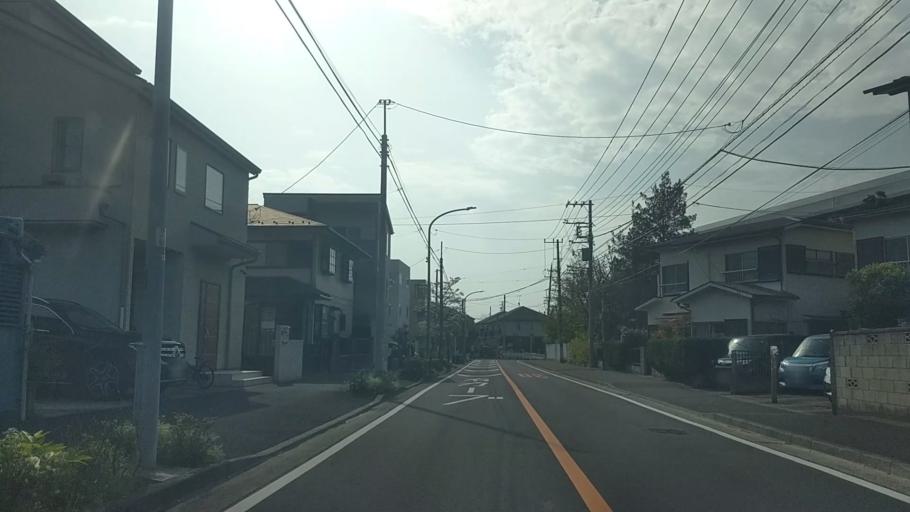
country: JP
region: Kanagawa
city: Kamakura
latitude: 35.3619
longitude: 139.5488
